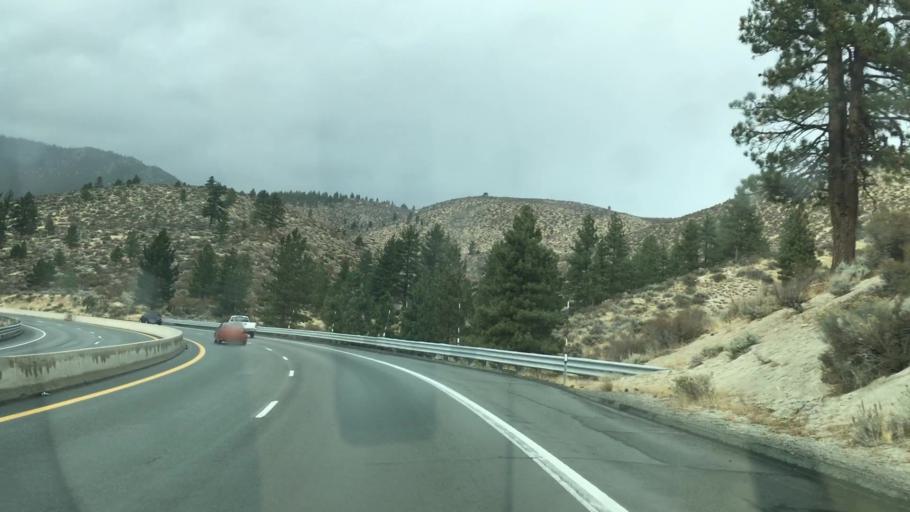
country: US
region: Nevada
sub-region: Douglas County
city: Indian Hills
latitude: 39.1201
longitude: -119.8164
